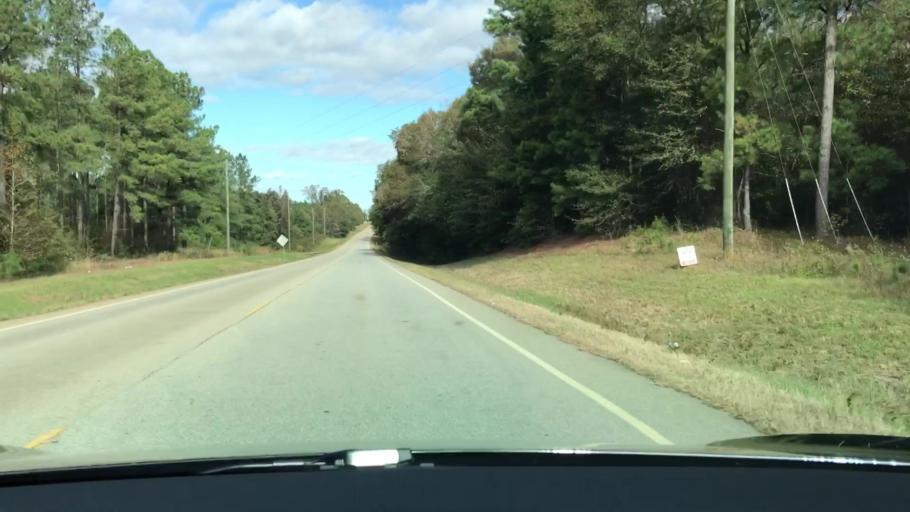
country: US
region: Georgia
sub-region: Jefferson County
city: Louisville
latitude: 33.0911
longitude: -82.4163
